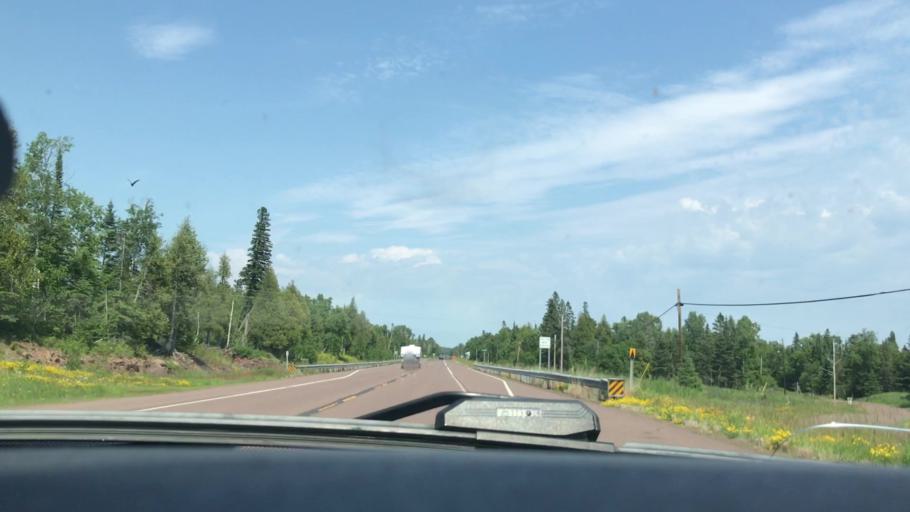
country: US
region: Minnesota
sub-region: Cook County
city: Grand Marais
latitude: 47.6273
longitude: -90.7340
